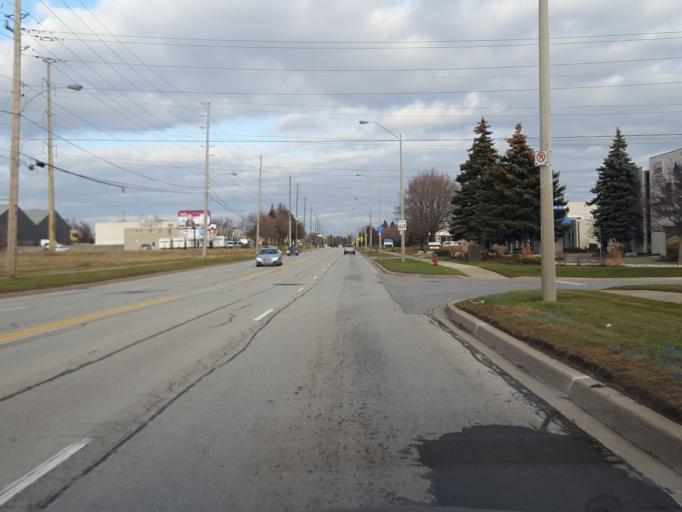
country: CA
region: Ontario
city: Burlington
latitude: 43.3542
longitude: -79.7963
